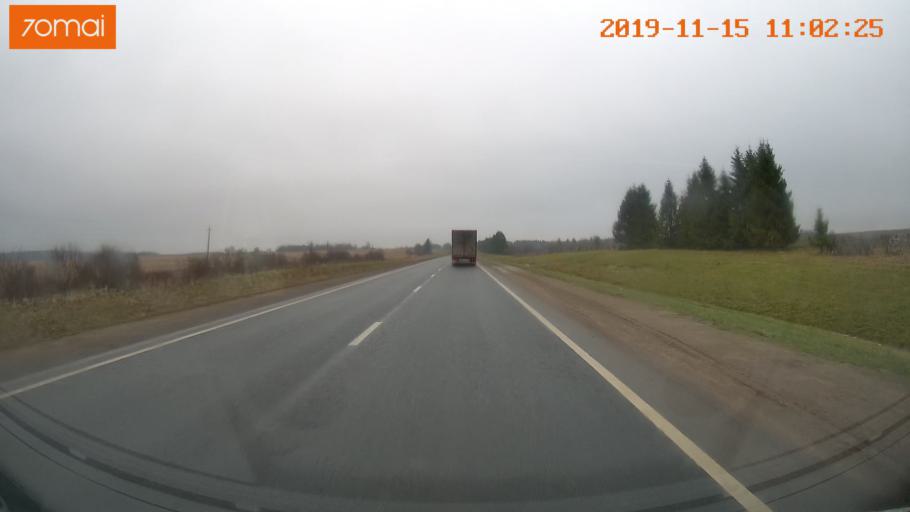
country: RU
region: Vologda
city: Chebsara
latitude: 59.1287
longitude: 38.9413
